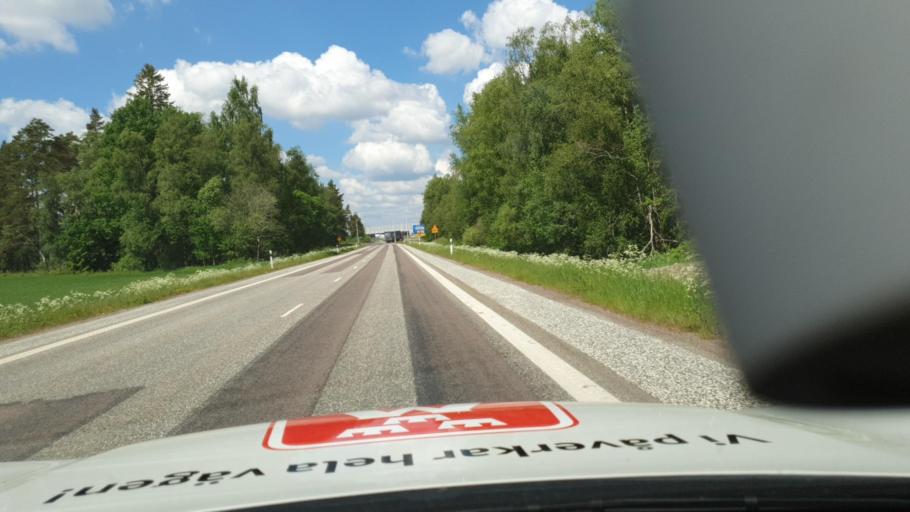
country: SE
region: Joenkoeping
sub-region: Jonkopings Kommun
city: Odensjo
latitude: 57.6437
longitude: 14.1999
